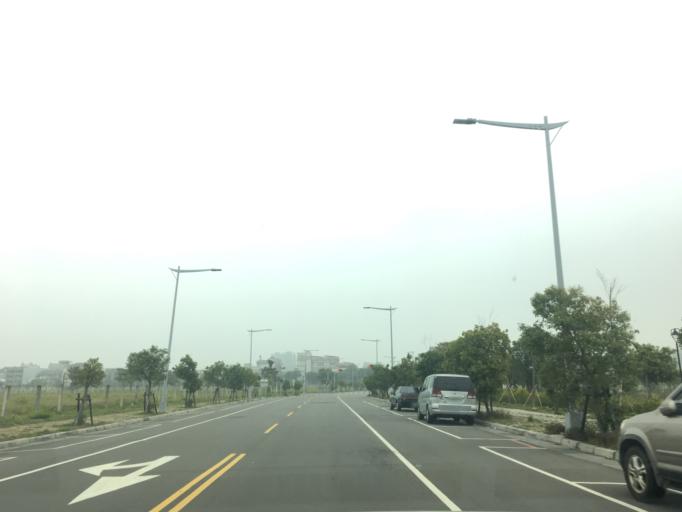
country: TW
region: Taiwan
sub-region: Taichung City
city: Taichung
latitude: 24.1933
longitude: 120.6724
